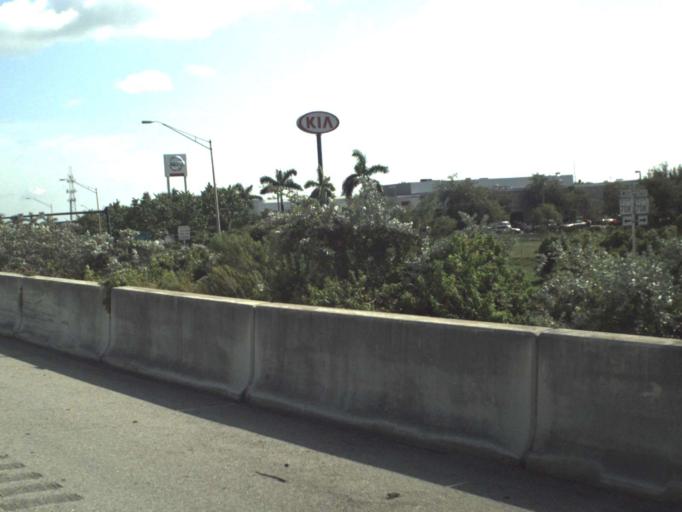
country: US
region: Florida
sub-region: Palm Beach County
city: Mangonia Park
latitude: 26.7804
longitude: -80.0989
